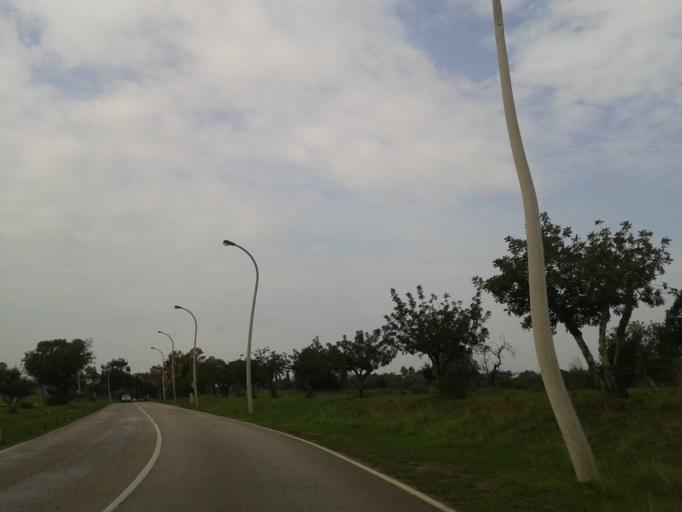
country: PT
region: Faro
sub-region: Loule
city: Boliqueime
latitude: 37.1114
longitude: -8.1468
